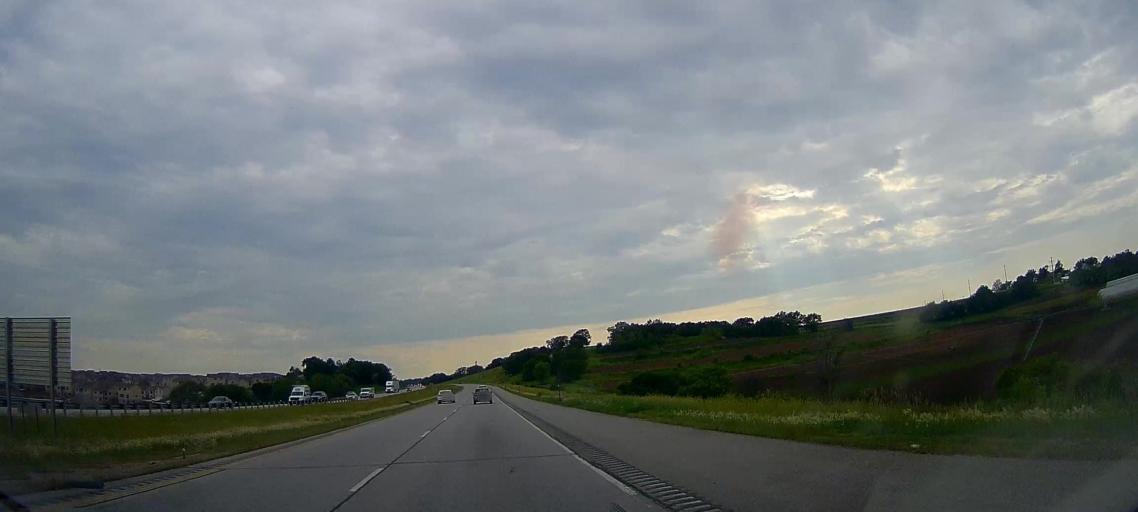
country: US
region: Nebraska
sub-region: Douglas County
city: Bennington
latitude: 41.3329
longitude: -96.0514
